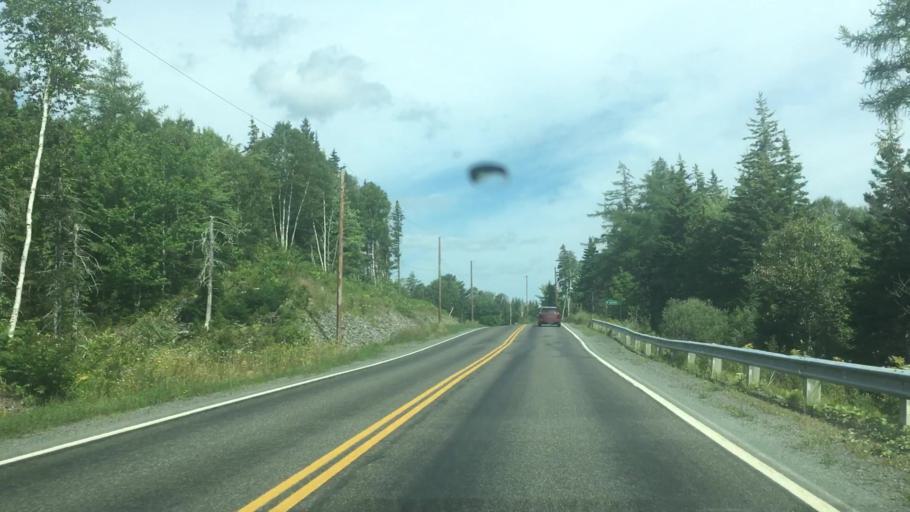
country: CA
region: Nova Scotia
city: Sydney Mines
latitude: 46.2112
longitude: -60.6207
